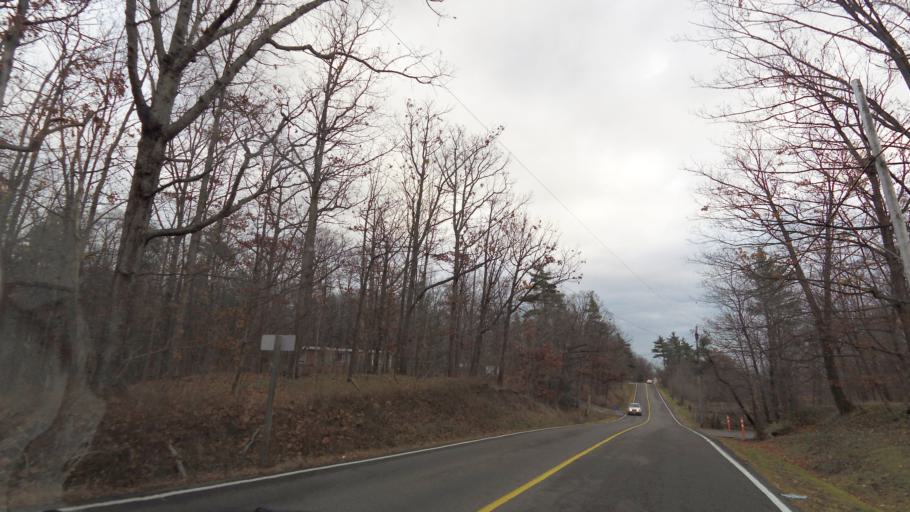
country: CA
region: Ontario
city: Burlington
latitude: 43.4052
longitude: -79.8417
